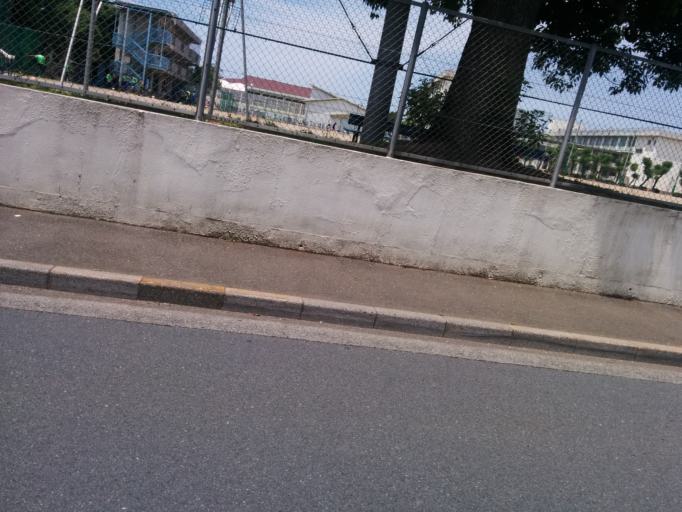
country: JP
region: Tokyo
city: Higashimurayama-shi
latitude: 35.7595
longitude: 139.4785
